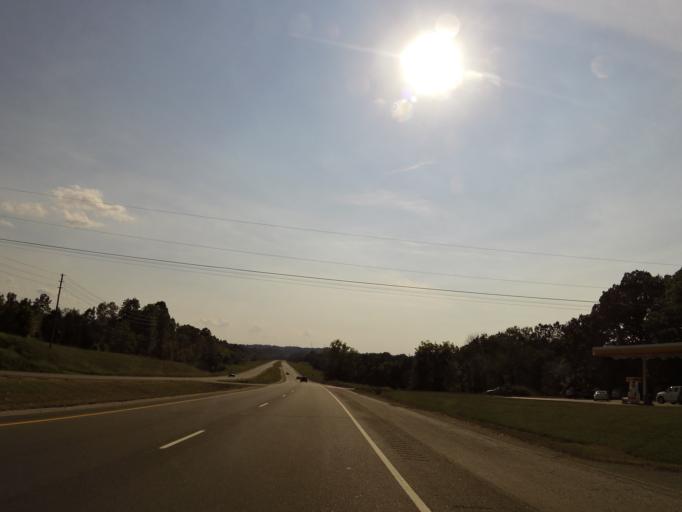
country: US
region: Tennessee
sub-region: Blount County
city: Louisville
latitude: 35.7563
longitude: -84.0916
